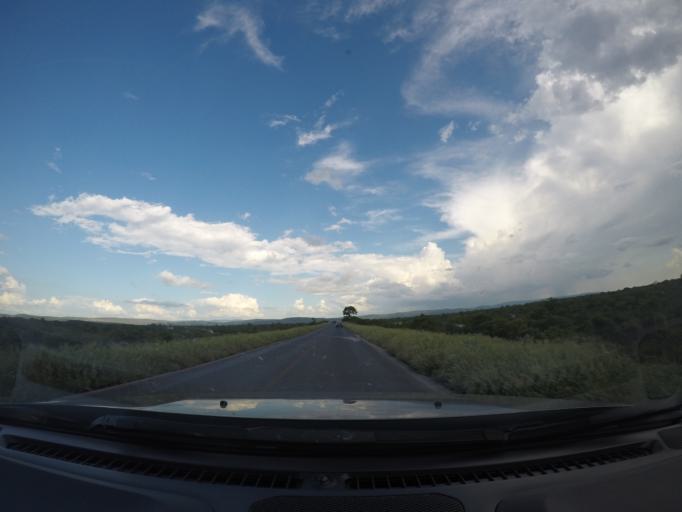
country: BR
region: Bahia
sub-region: Ibotirama
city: Ibotirama
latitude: -12.1698
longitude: -43.2670
